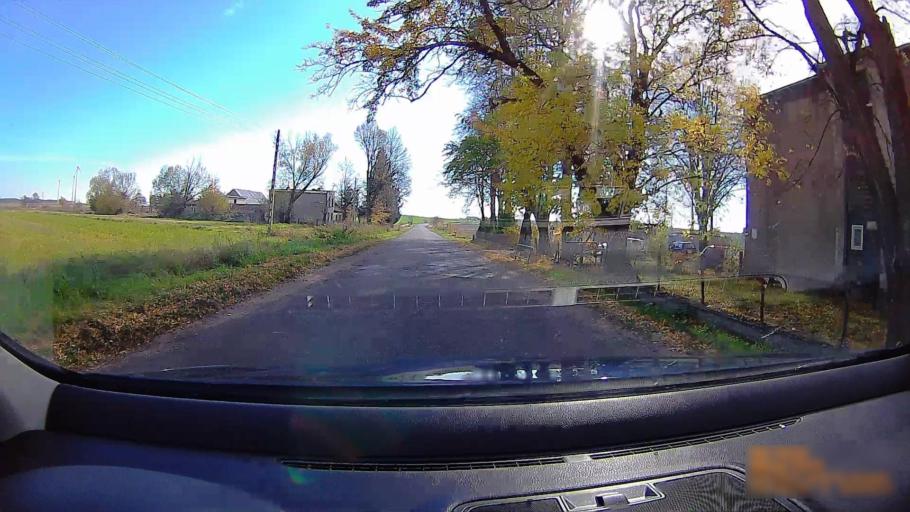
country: PL
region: Greater Poland Voivodeship
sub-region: Powiat ostrzeszowski
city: Doruchow
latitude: 51.4014
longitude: 18.0282
